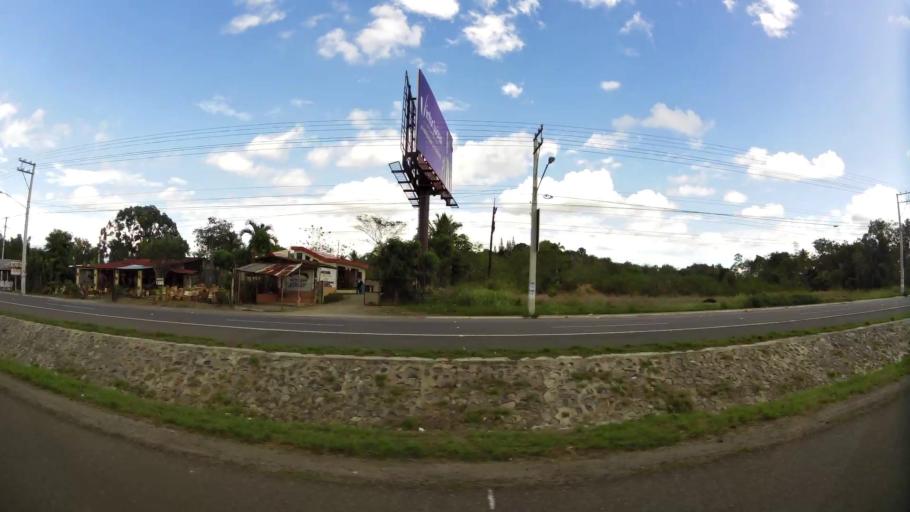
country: DO
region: La Vega
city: Rio Verde Arriba
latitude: 19.3483
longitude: -70.6003
